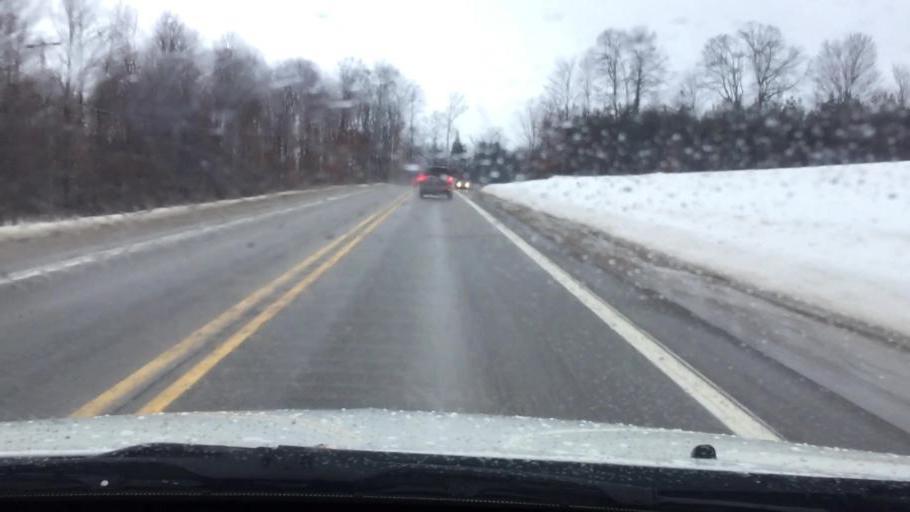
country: US
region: Michigan
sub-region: Charlevoix County
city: East Jordan
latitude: 45.1949
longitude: -85.1646
